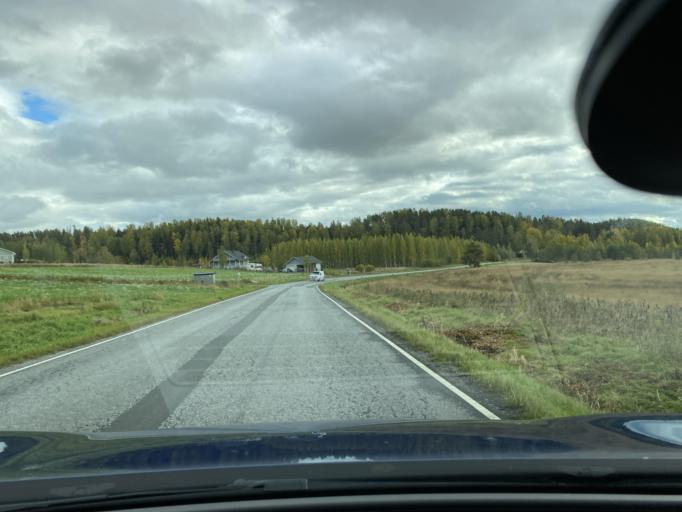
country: FI
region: Pirkanmaa
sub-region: Tampere
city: Nokia
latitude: 61.5001
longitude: 23.3440
